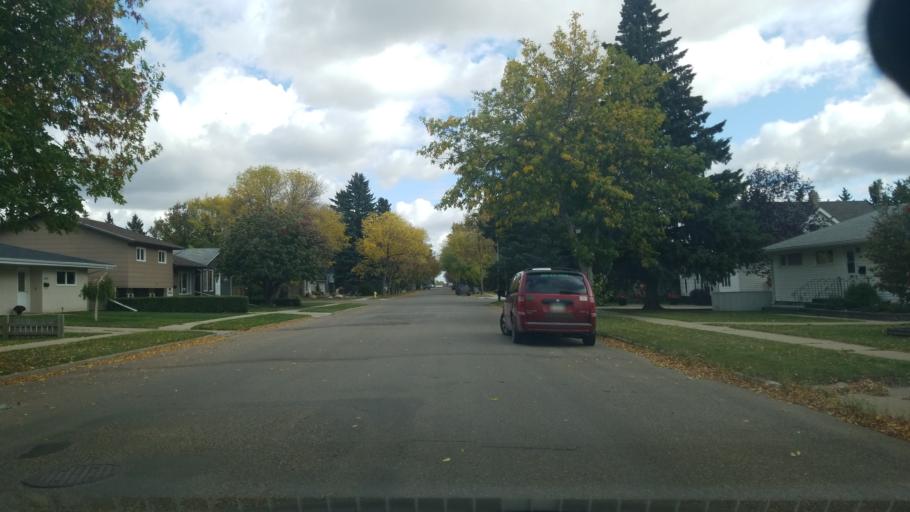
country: CA
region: Saskatchewan
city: Lloydminster
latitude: 53.2807
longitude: -110.0169
